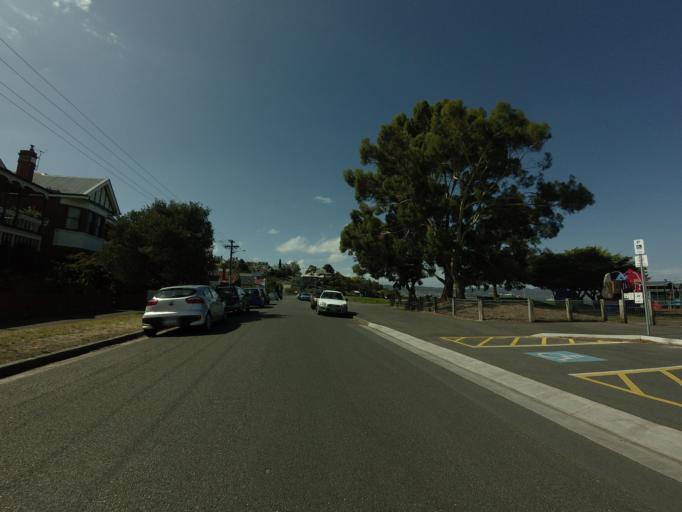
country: AU
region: Tasmania
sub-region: Hobart
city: Sandy Bay
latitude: -42.8958
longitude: 147.3326
